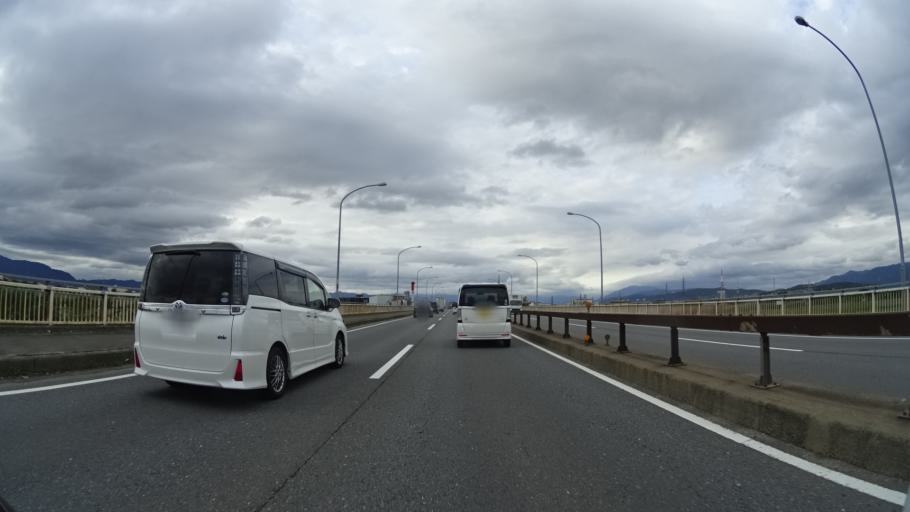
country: JP
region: Kyoto
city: Yawata
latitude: 34.9164
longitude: 135.7446
